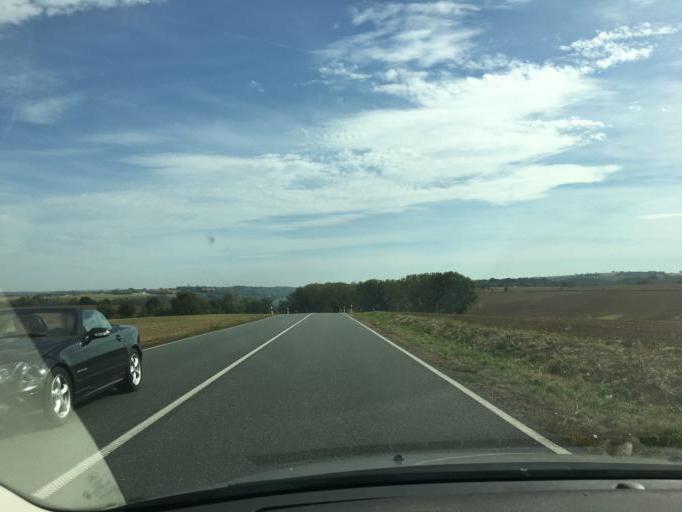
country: DE
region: Saxony
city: Lommatzsch
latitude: 51.2057
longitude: 13.3900
